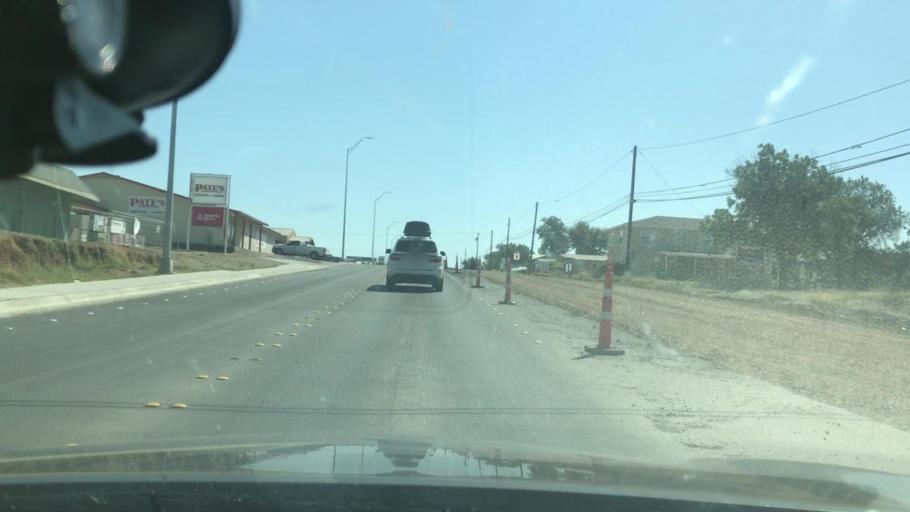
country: US
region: Texas
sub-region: Stephens County
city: Breckenridge
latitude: 32.7555
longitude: -98.8938
